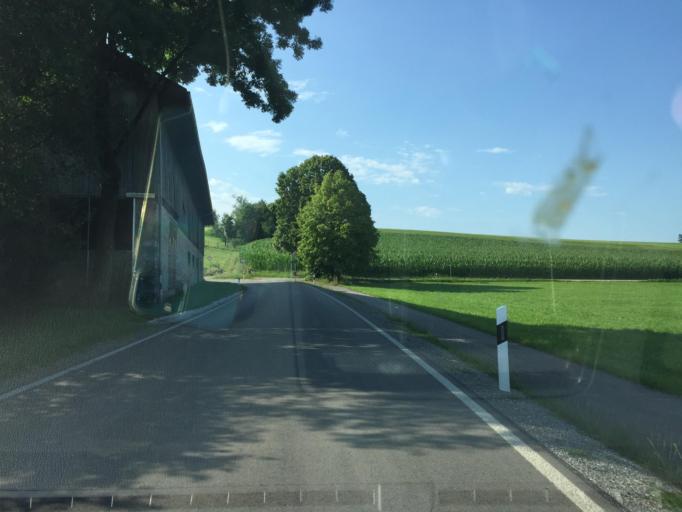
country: DE
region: Bavaria
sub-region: Upper Bavaria
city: Tuntenhausen
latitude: 47.9525
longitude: 12.0204
